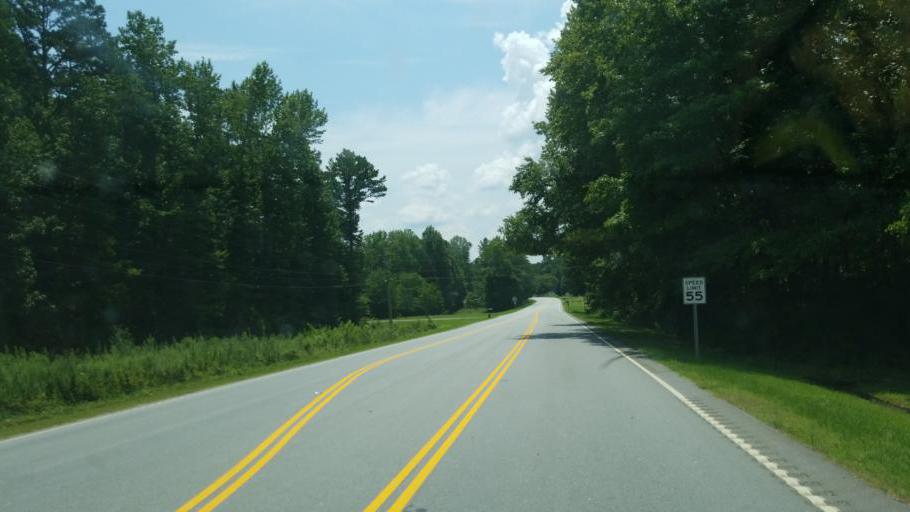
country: US
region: North Carolina
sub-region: Cleveland County
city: Kings Mountain
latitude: 35.1596
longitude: -81.3268
